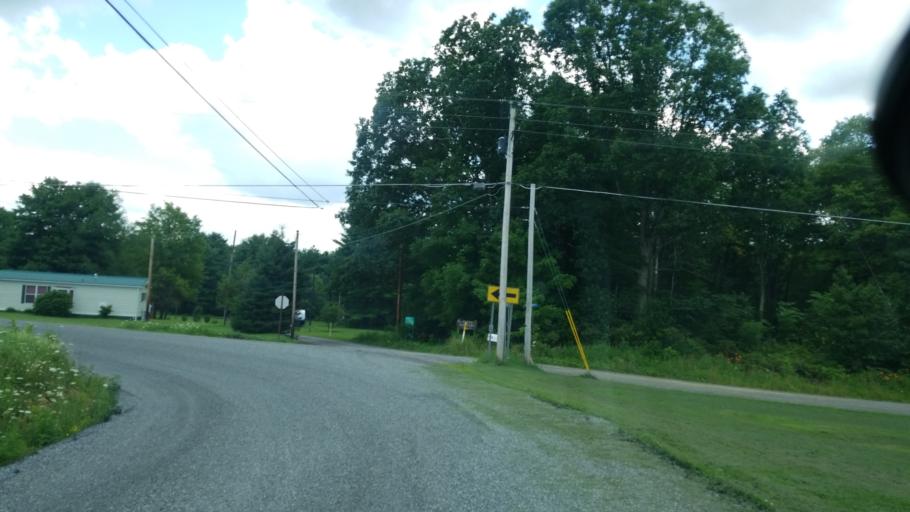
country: US
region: Pennsylvania
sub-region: Jefferson County
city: Brookville
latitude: 41.2324
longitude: -79.0116
